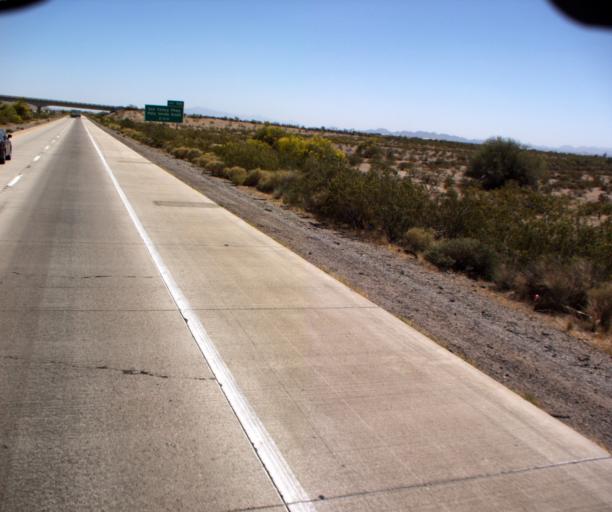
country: US
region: Arizona
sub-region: Maricopa County
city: Buckeye
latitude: 33.4477
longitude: -112.7156
